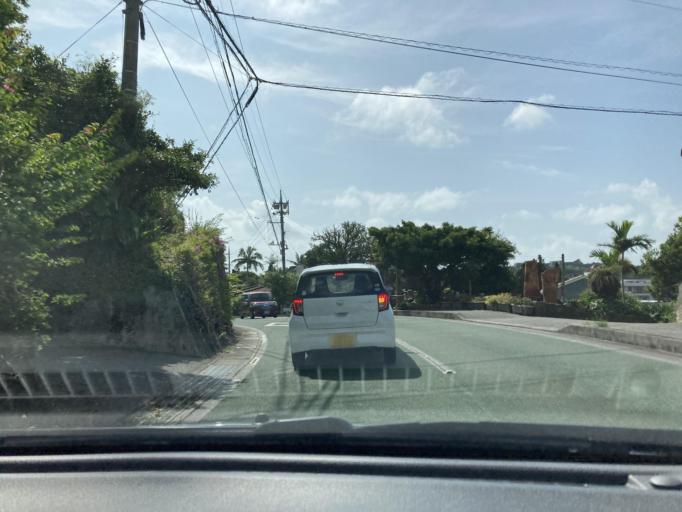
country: JP
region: Okinawa
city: Chatan
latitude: 26.2907
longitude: 127.8003
